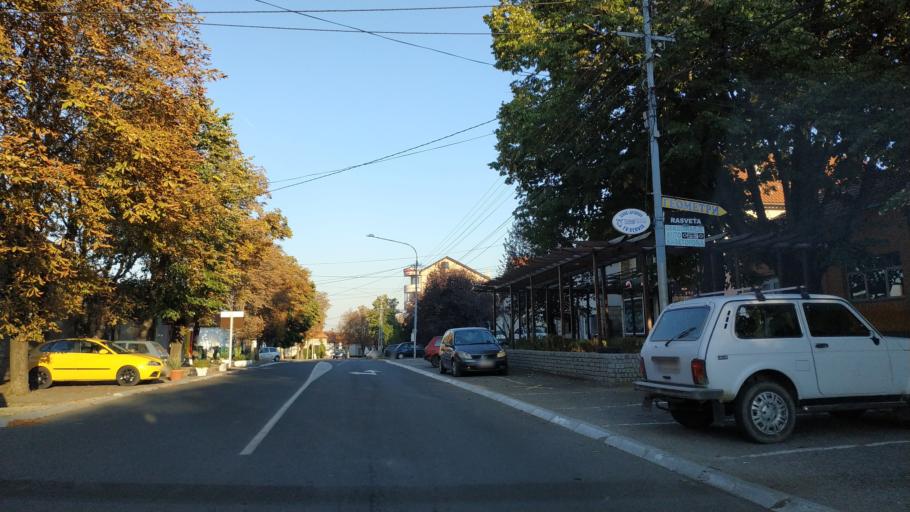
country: RS
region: Central Serbia
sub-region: Sumadijski Okrug
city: Topola
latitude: 44.2544
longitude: 20.6816
